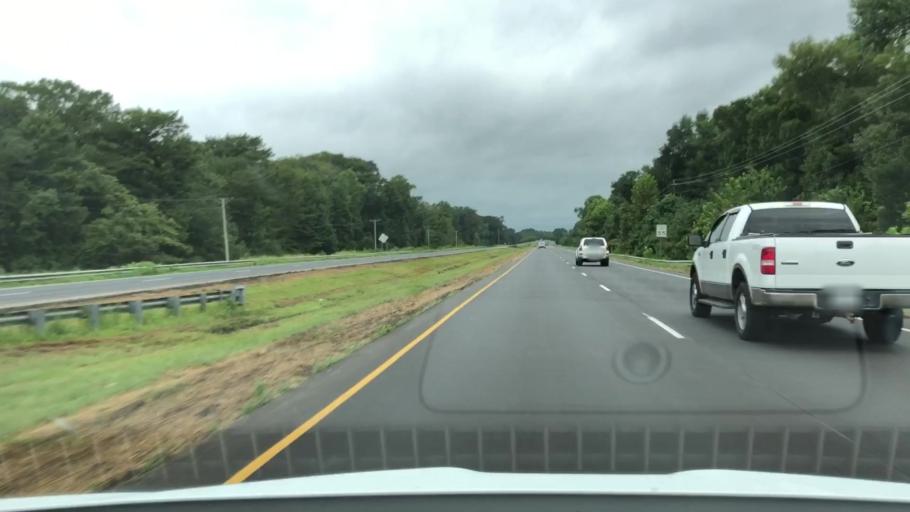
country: US
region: North Carolina
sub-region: Lenoir County
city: Kinston
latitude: 35.2616
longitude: -77.6199
